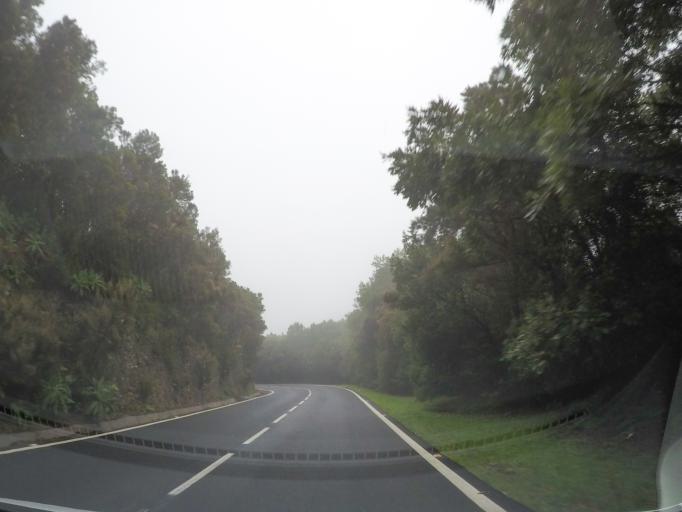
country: ES
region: Canary Islands
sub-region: Provincia de Santa Cruz de Tenerife
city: Vallehermosa
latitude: 28.1261
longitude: -17.2561
